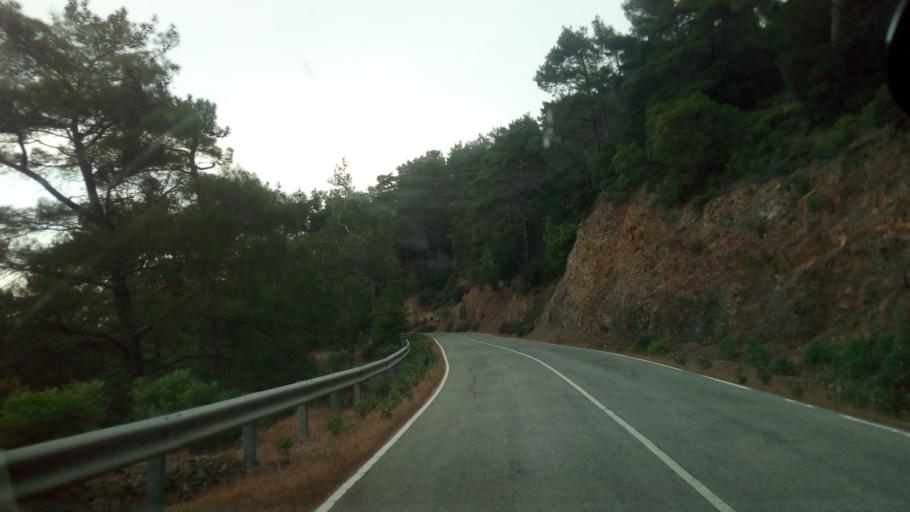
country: CY
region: Lefkosia
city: Lefka
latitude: 35.0092
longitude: 32.7283
